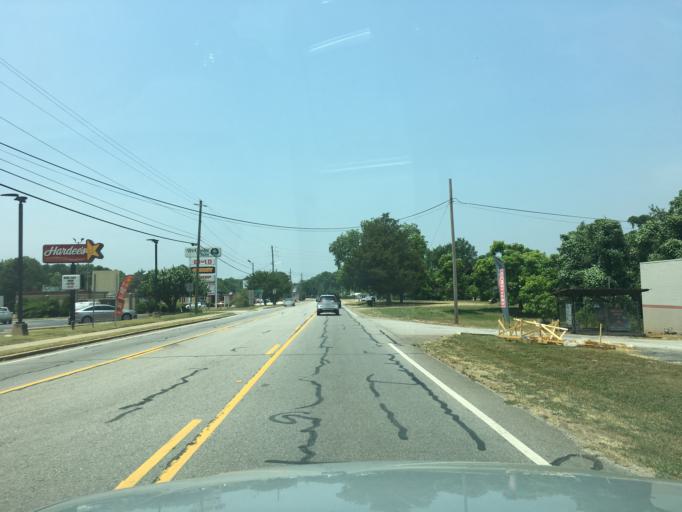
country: US
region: Georgia
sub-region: Hart County
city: Royston
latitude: 34.2850
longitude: -83.1269
